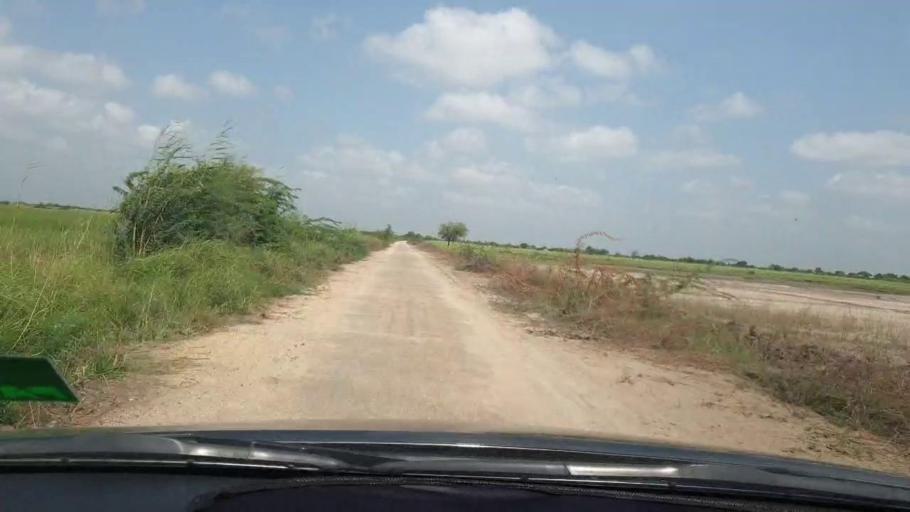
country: PK
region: Sindh
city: Tando Bago
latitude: 24.8675
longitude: 69.0355
